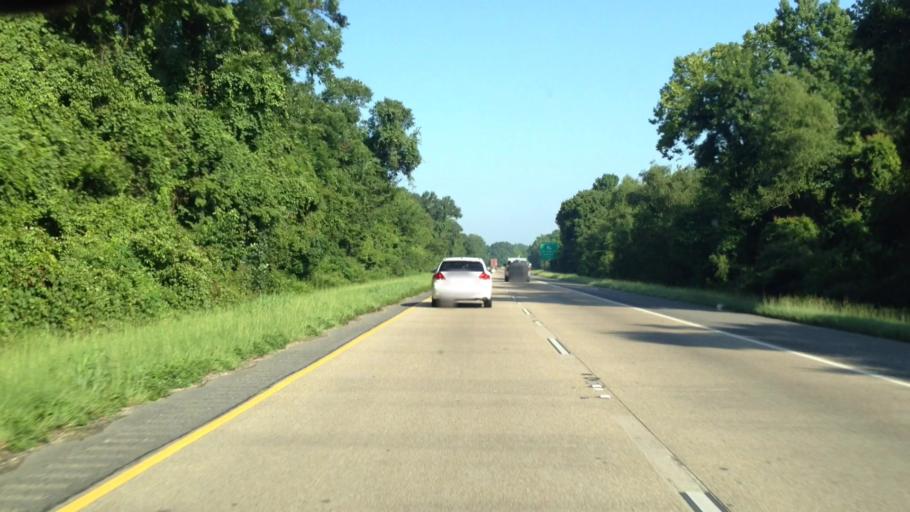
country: US
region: Louisiana
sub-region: Ascension Parish
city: Gonzales
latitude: 30.1969
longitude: -90.9288
